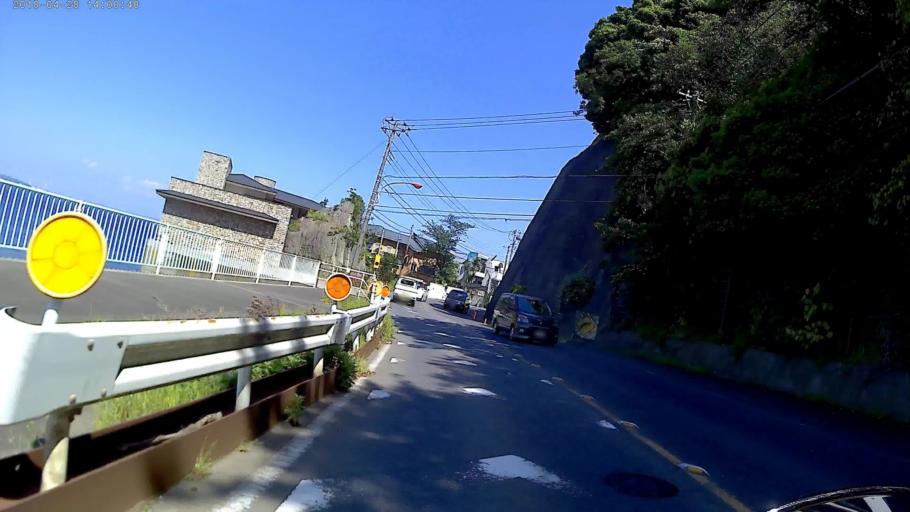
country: JP
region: Kanagawa
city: Miura
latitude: 35.1718
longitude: 139.6583
